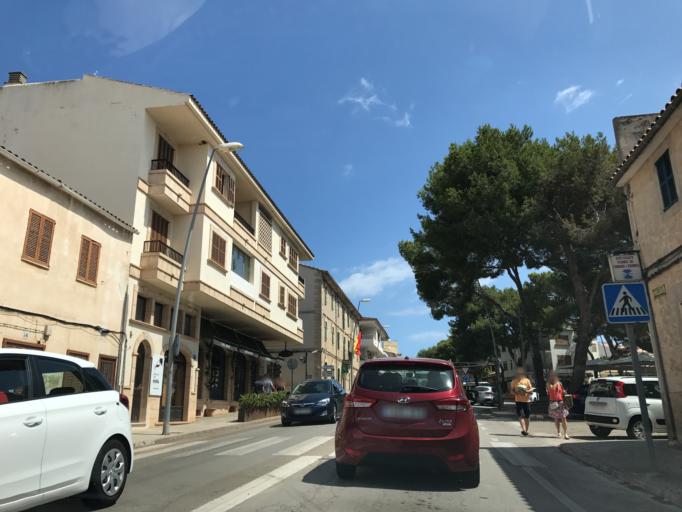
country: ES
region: Balearic Islands
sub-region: Illes Balears
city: Arta
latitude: 39.6907
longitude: 3.3477
